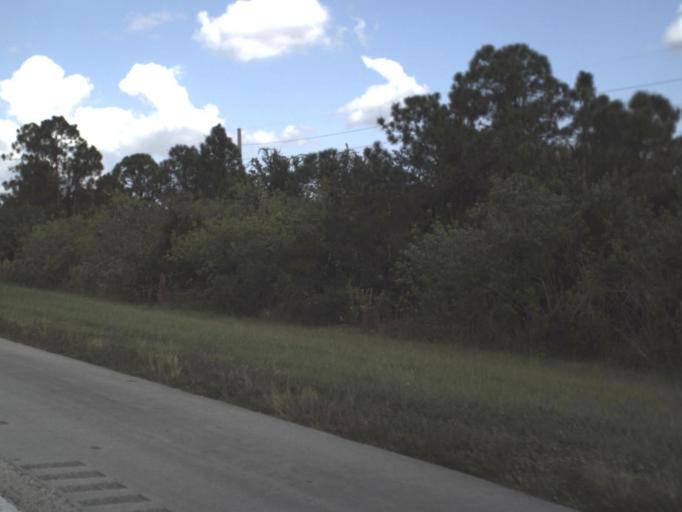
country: US
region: Florida
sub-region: Martin County
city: Palm City
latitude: 27.1315
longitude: -80.2843
